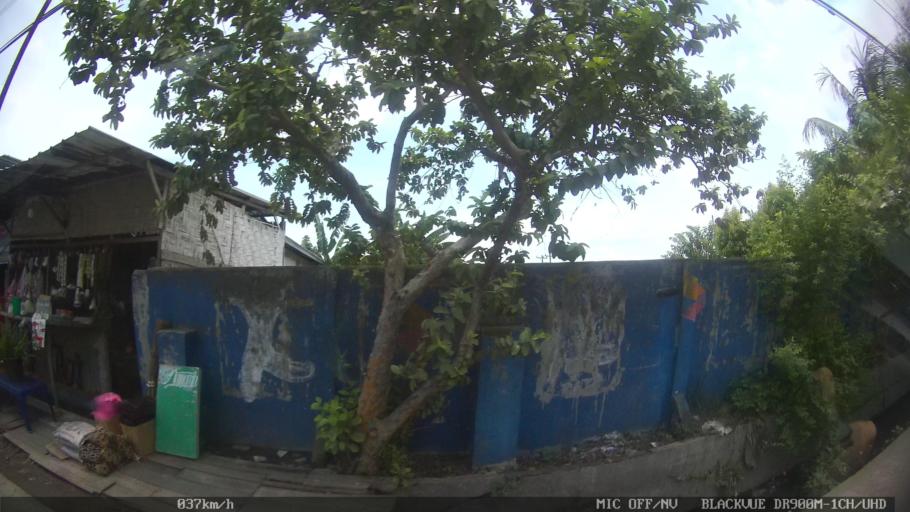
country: ID
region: North Sumatra
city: Labuhan Deli
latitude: 3.6850
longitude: 98.6906
